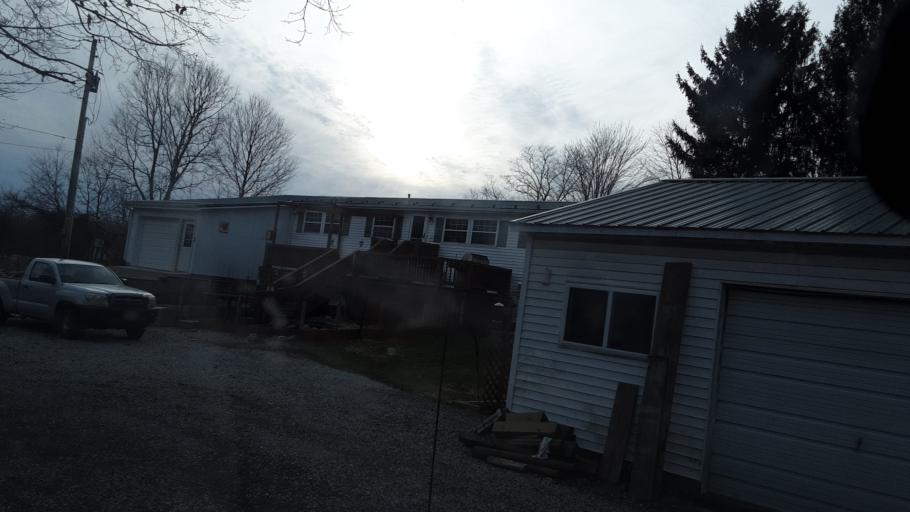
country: US
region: Ohio
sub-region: Knox County
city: Fredericktown
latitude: 40.4801
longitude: -82.6860
